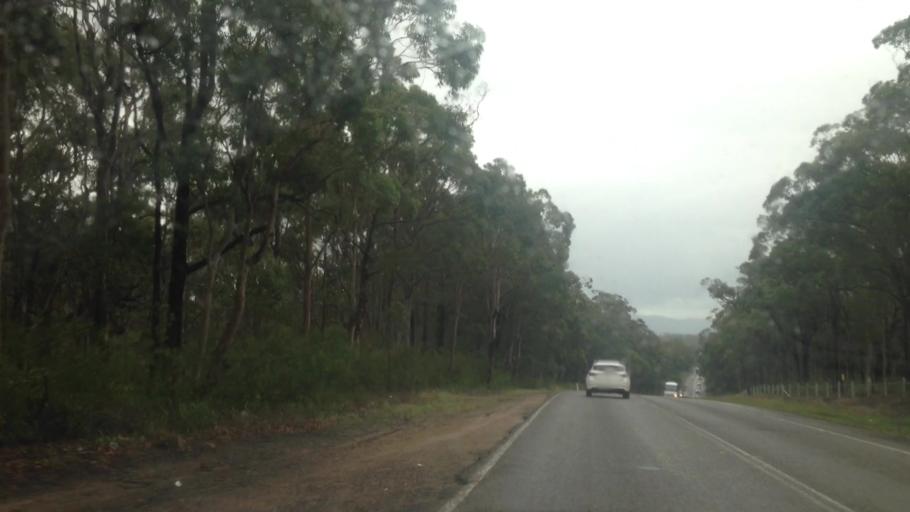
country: AU
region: New South Wales
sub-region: Lake Macquarie Shire
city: Dora Creek
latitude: -33.1432
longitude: 151.4781
